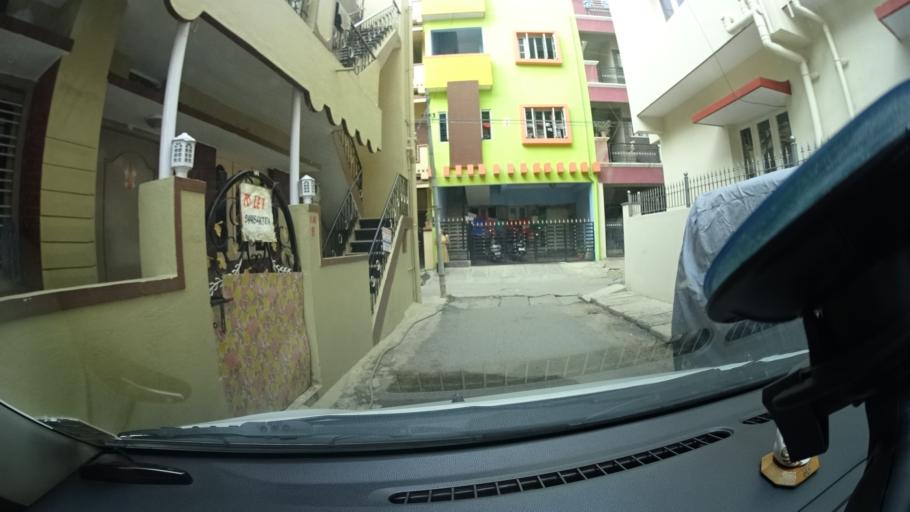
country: IN
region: Karnataka
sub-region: Bangalore Urban
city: Yelahanka
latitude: 13.0931
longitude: 77.5805
